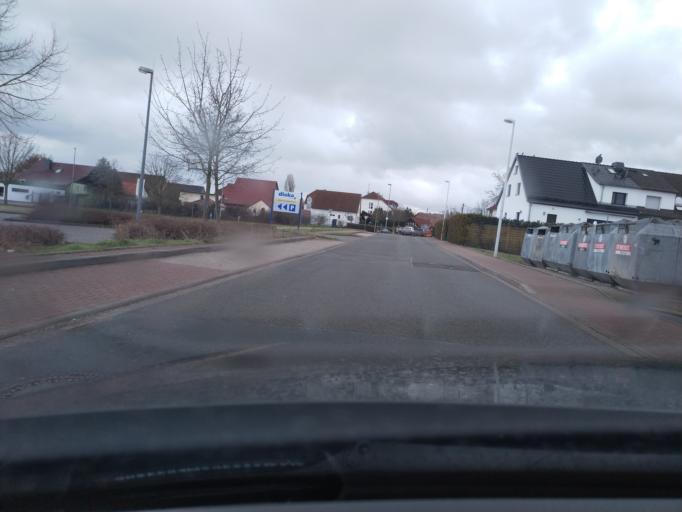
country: DE
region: Thuringia
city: Kleinmolsen
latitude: 51.0098
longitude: 11.1020
